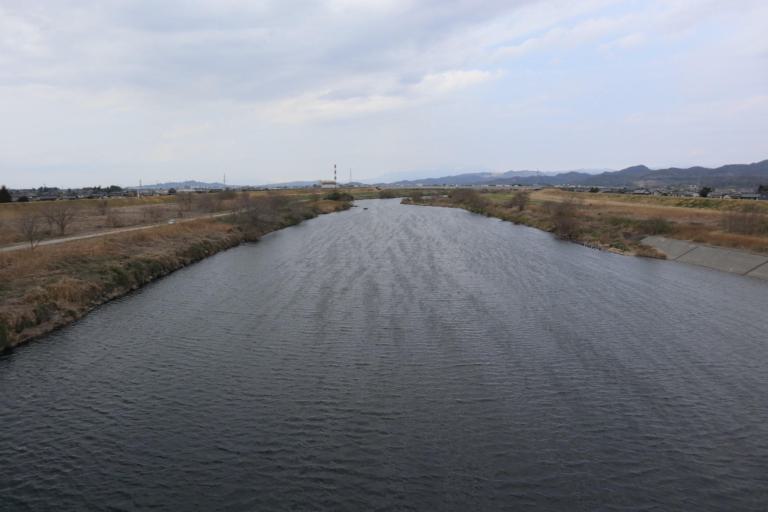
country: JP
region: Gunma
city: Tatebayashi
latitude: 36.2826
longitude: 139.5351
